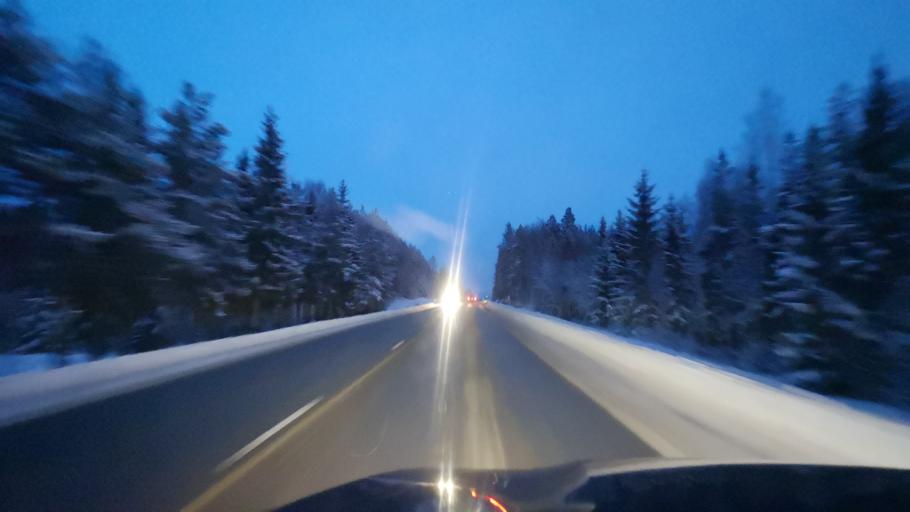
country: FI
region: Varsinais-Suomi
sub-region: Loimaa
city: Loimaa
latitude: 60.8681
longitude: 23.0569
